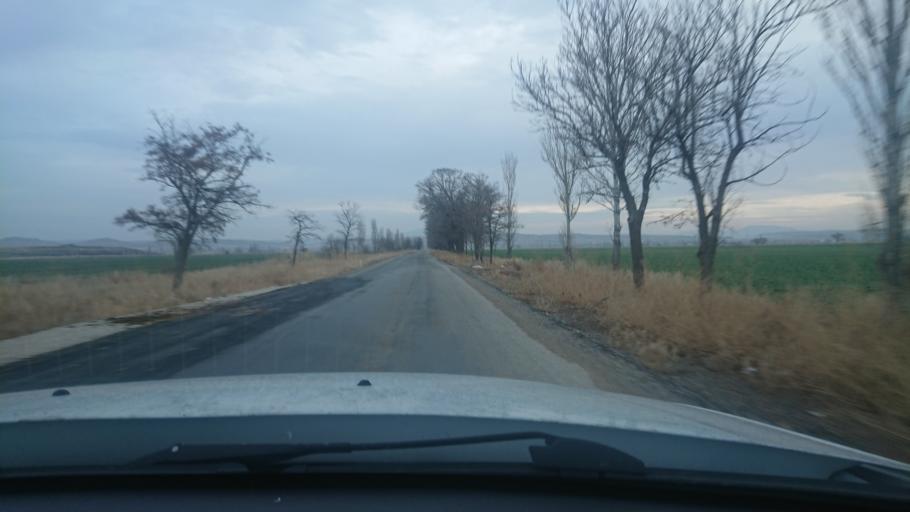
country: TR
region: Aksaray
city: Yesilova
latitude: 38.4631
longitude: 33.8425
